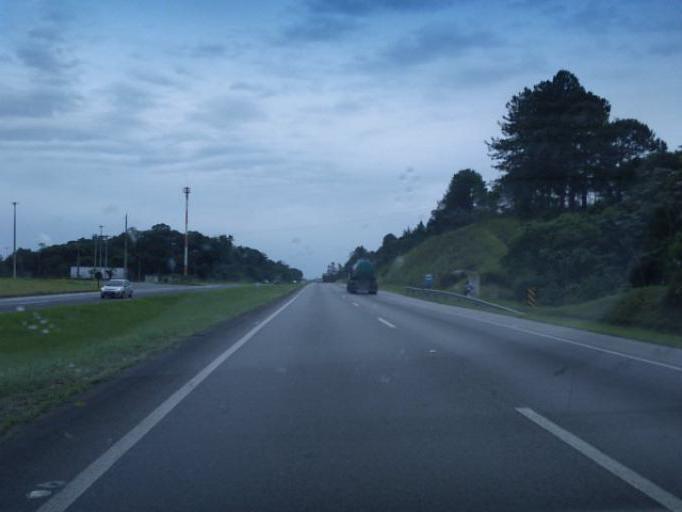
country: BR
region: Sao Paulo
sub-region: Registro
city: Registro
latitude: -24.4450
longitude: -47.8025
